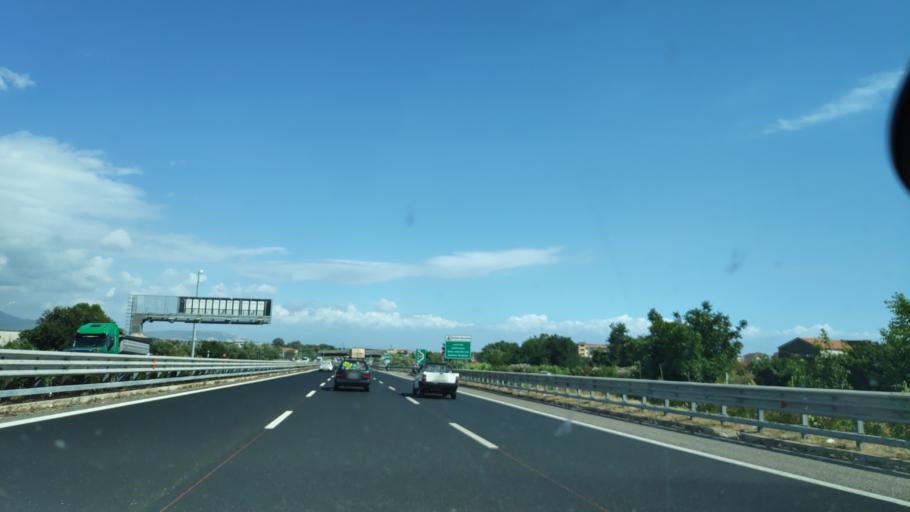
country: IT
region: Campania
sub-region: Provincia di Salerno
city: Pontecagnano
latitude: 40.6543
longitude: 14.8693
